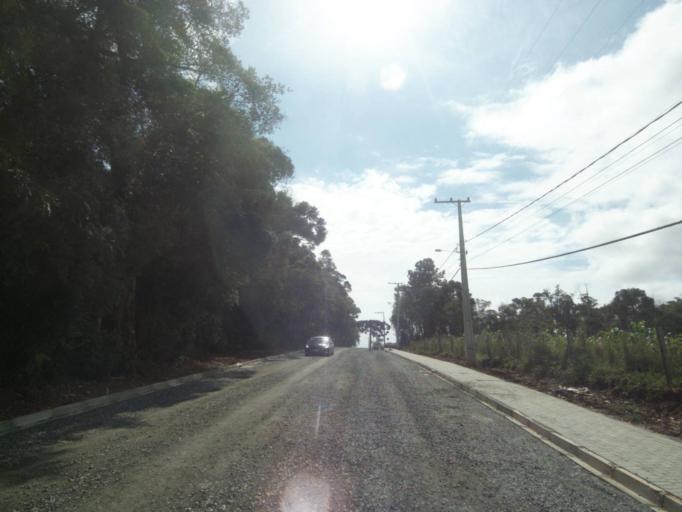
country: BR
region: Parana
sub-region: Quatro Barras
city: Quatro Barras
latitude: -25.3337
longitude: -49.0730
